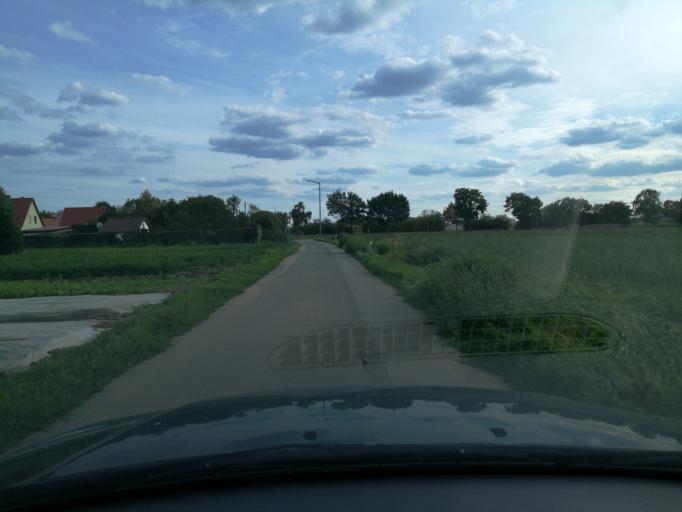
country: DE
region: Bavaria
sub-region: Regierungsbezirk Mittelfranken
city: Wetzendorf
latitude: 49.4862
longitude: 11.0642
